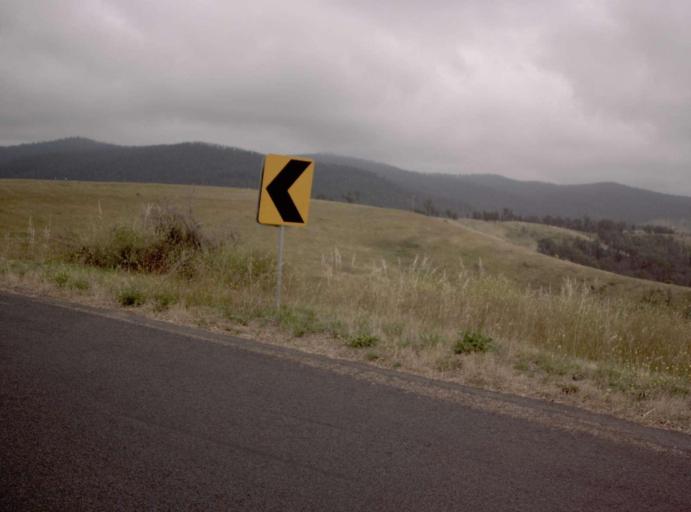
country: AU
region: Victoria
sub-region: Wellington
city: Heyfield
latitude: -37.8379
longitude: 146.6885
